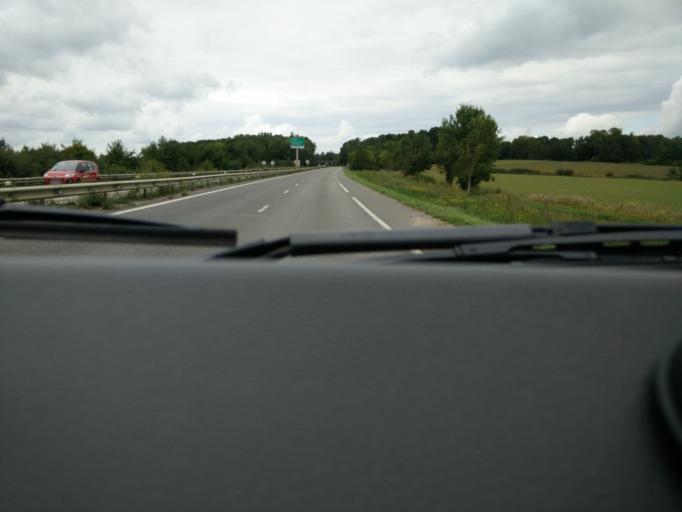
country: FR
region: Champagne-Ardenne
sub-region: Departement des Ardennes
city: Bazeilles
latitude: 49.6799
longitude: 4.9992
